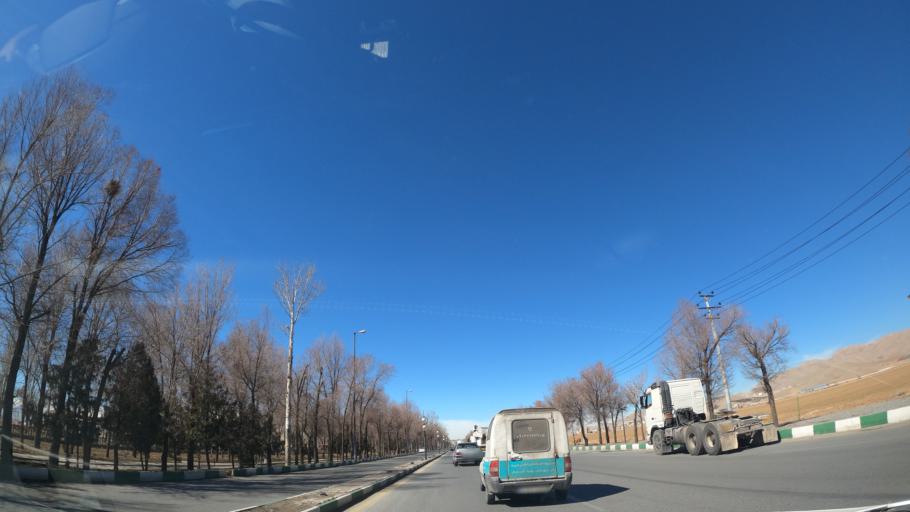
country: IR
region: Chahar Mahall va Bakhtiari
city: Shahrekord
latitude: 32.3079
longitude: 50.9006
